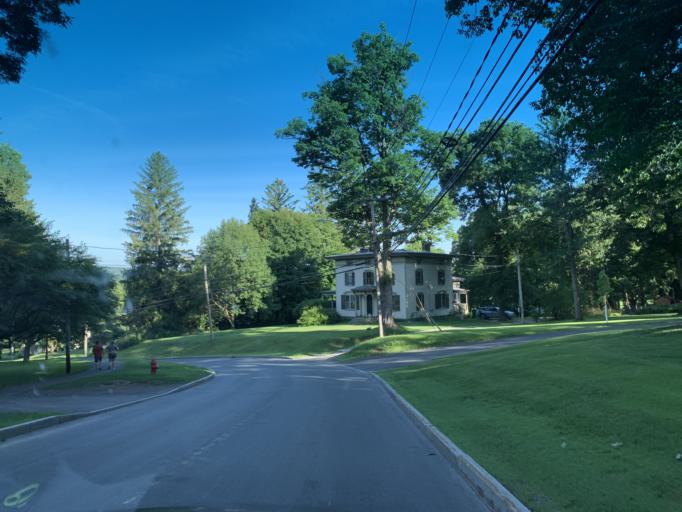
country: US
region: New York
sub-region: Oneida County
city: Clinton
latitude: 43.0489
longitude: -75.3977
